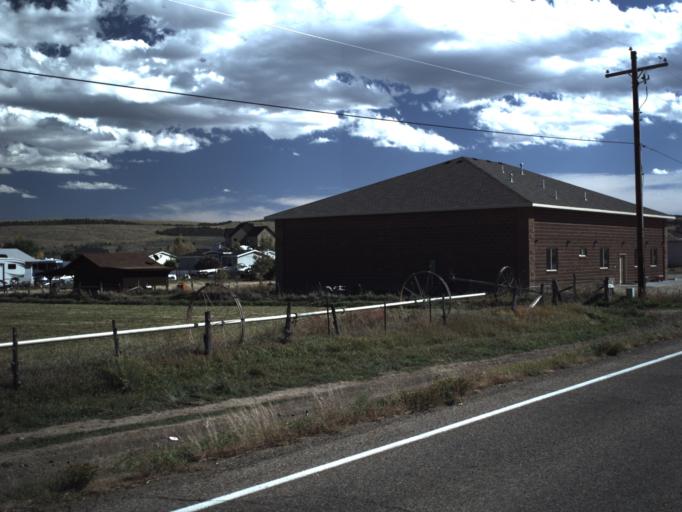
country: US
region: Utah
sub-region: Garfield County
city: Panguitch
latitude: 37.8107
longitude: -112.4355
